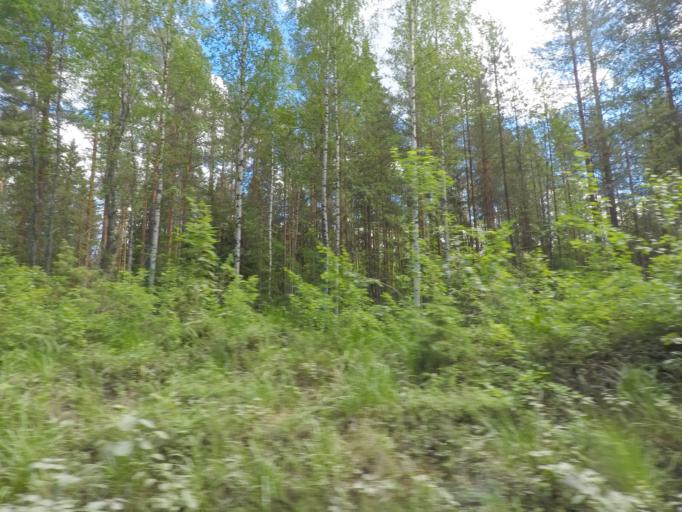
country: FI
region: Central Finland
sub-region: Jyvaeskylae
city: Hankasalmi
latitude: 62.4341
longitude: 26.6481
